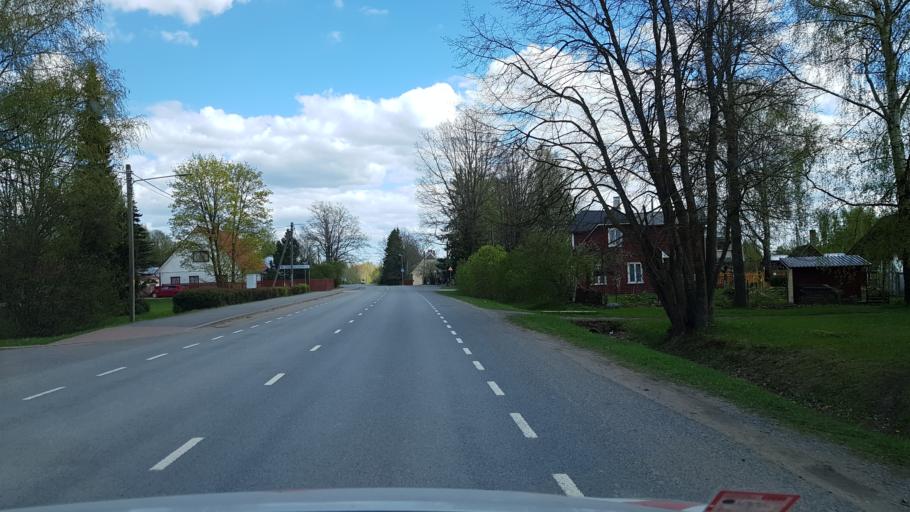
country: EE
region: Polvamaa
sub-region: Polva linn
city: Polva
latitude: 58.2834
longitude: 27.0461
